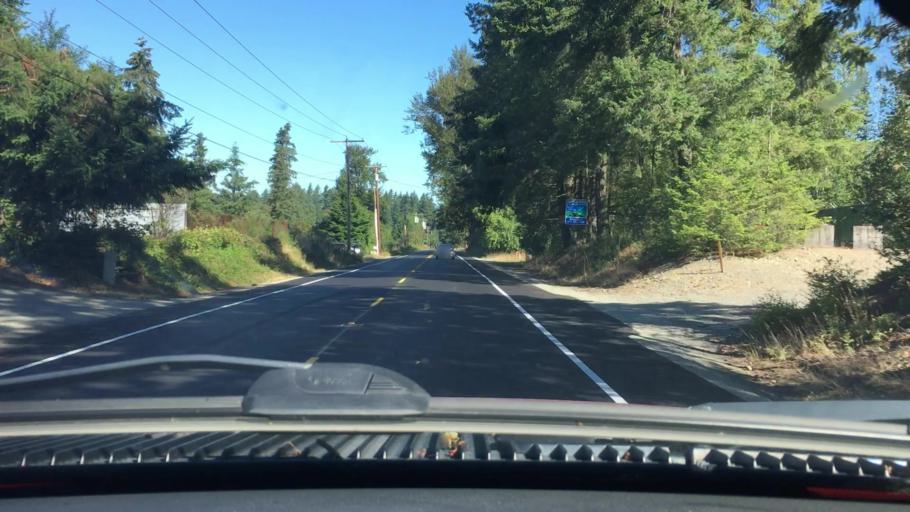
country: US
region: Washington
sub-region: King County
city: Lake Morton-Berrydale
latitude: 47.3223
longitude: -122.1083
